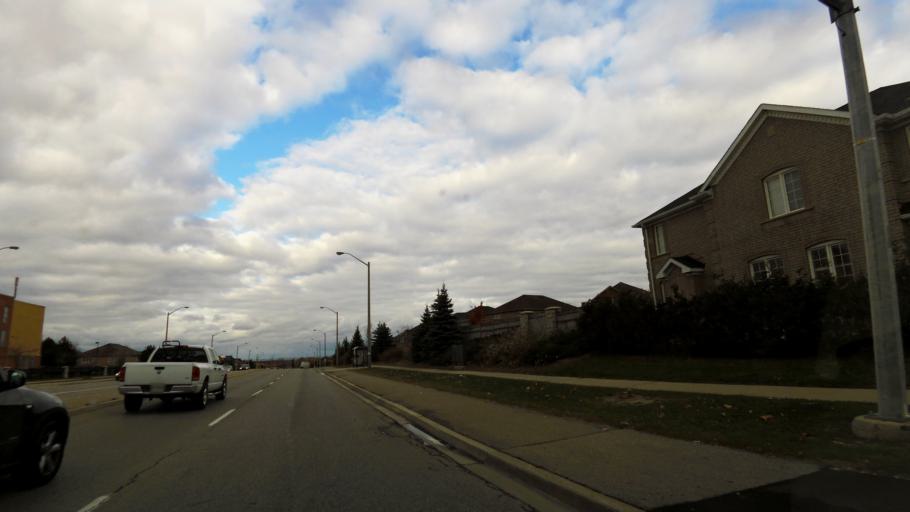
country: CA
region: Ontario
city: Brampton
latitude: 43.7575
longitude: -79.7543
